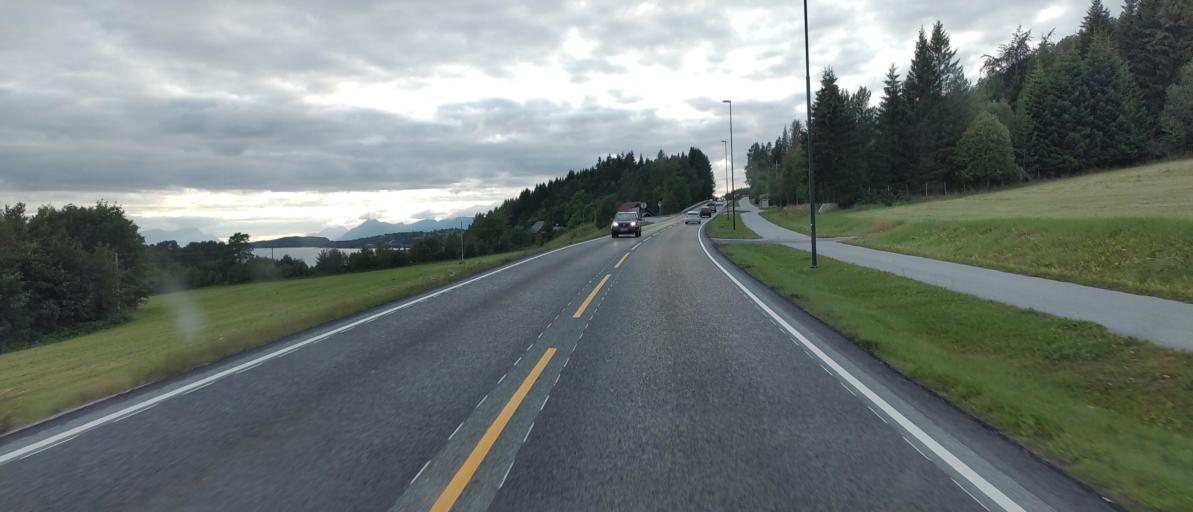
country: NO
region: More og Romsdal
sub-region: Molde
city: Hjelset
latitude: 62.7330
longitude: 7.4055
